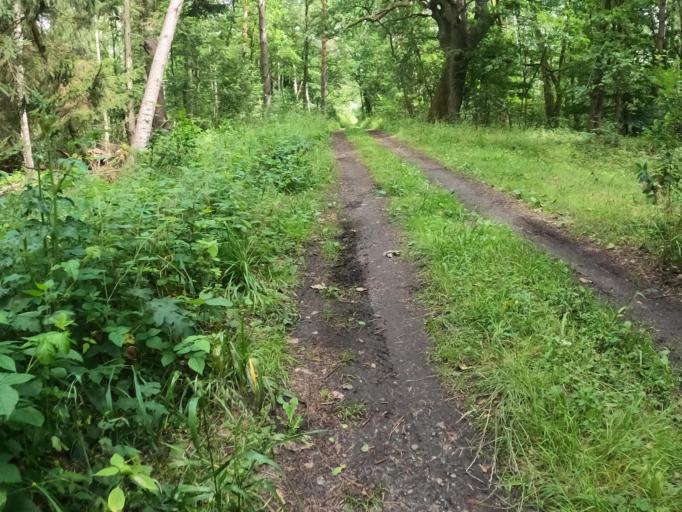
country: PL
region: West Pomeranian Voivodeship
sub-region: Powiat bialogardzki
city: Bialogard
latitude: 53.9929
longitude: 15.9339
